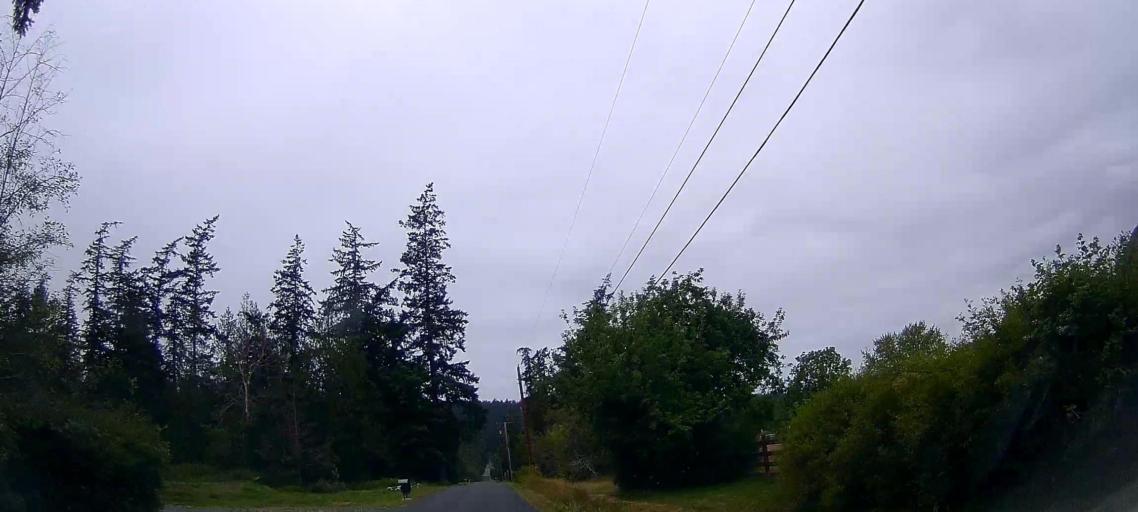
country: US
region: Washington
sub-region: Skagit County
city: Anacortes
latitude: 48.4336
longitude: -122.6115
